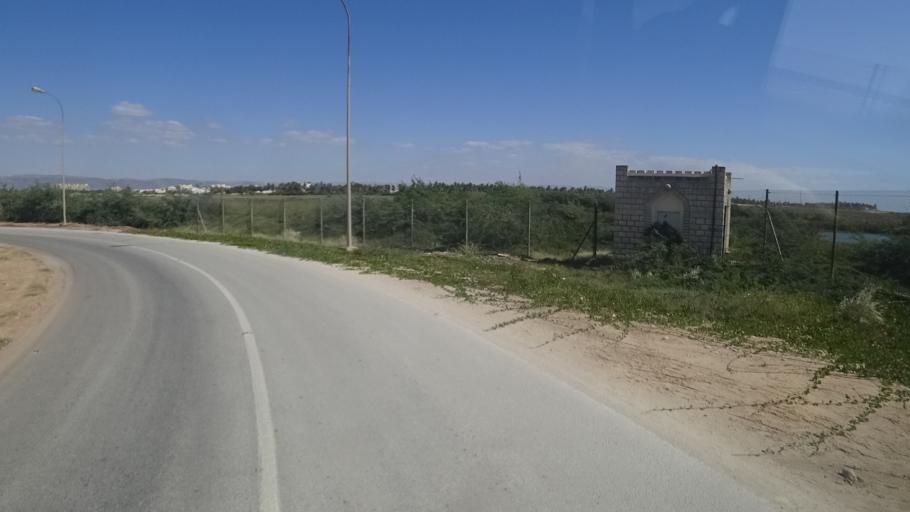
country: OM
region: Zufar
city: Salalah
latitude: 16.9953
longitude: 54.0656
